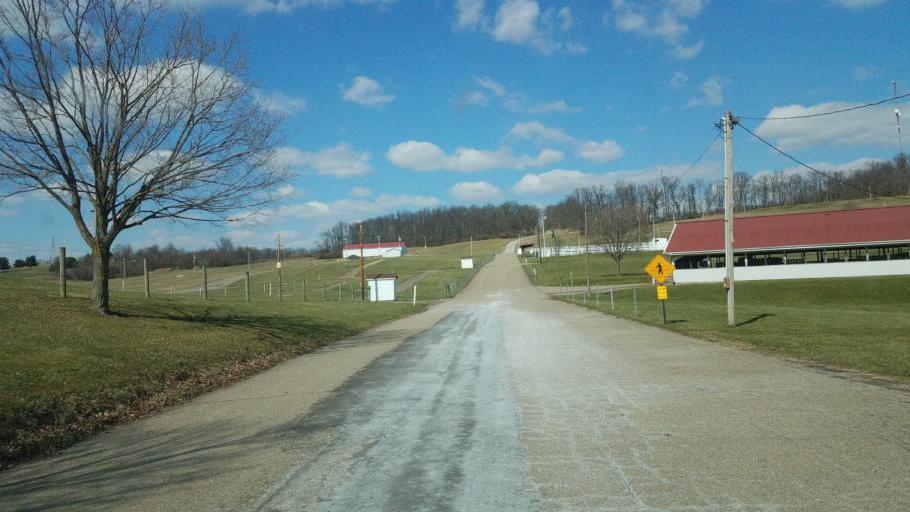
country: US
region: Ohio
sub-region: Knox County
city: Mount Vernon
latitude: 40.4166
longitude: -82.4760
